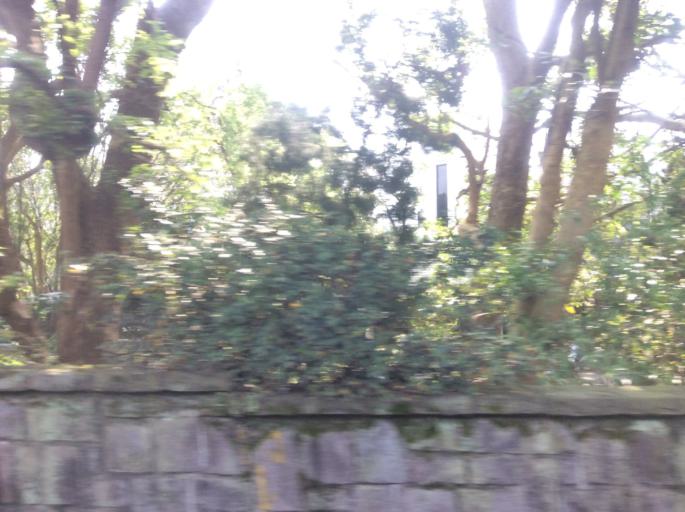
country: TW
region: Taipei
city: Taipei
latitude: 25.1352
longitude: 121.5461
